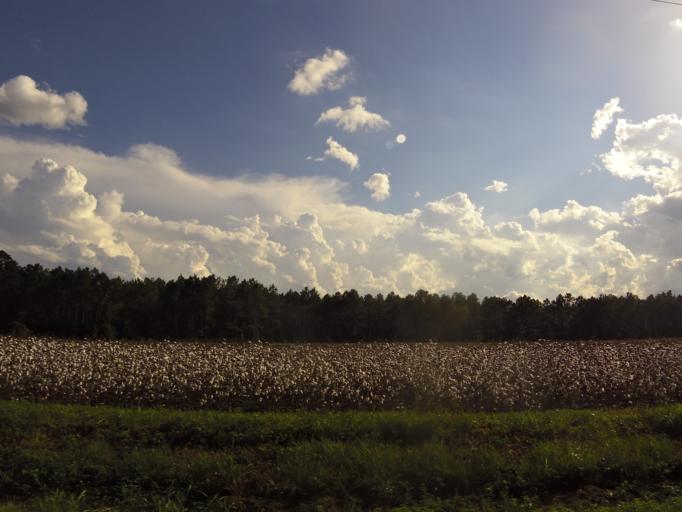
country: US
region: Georgia
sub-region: Brooks County
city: Quitman
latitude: 30.7843
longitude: -83.6270
